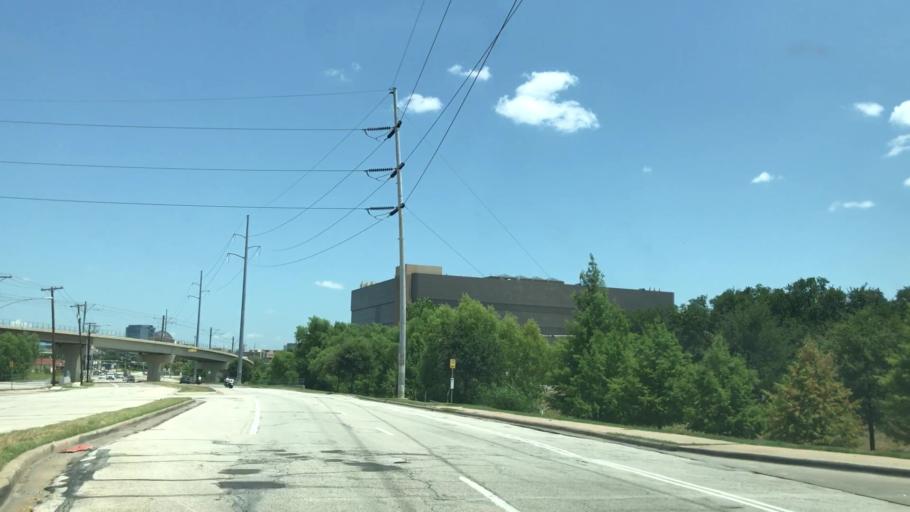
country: US
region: Texas
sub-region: Dallas County
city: Dallas
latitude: 32.8059
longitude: -96.8295
